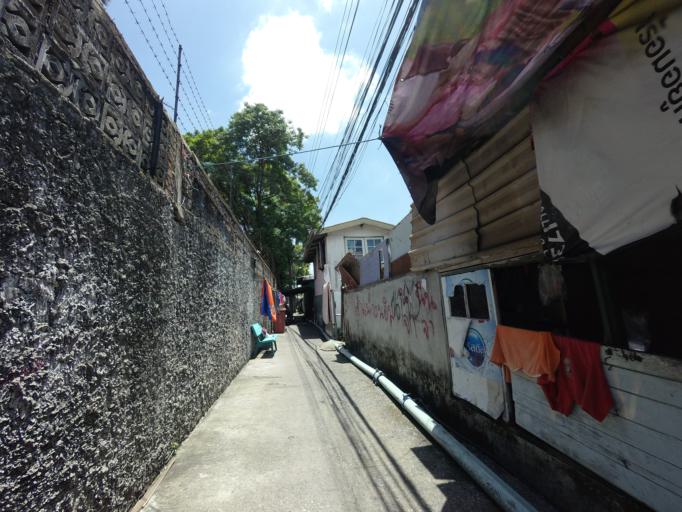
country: TH
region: Bangkok
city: Lat Phrao
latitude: 13.8061
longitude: 100.5884
